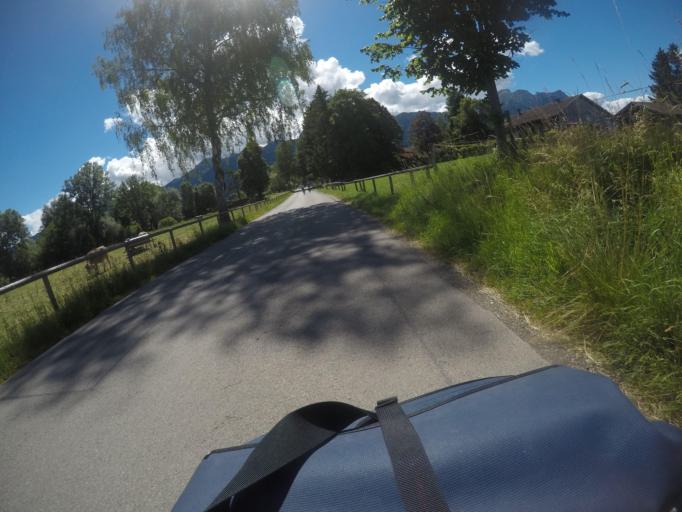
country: DE
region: Bavaria
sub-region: Swabia
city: Schwangau
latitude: 47.5925
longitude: 10.7414
